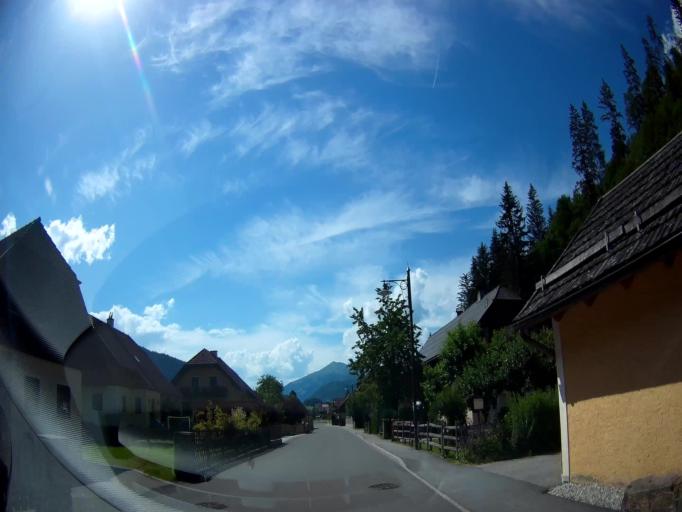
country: AT
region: Salzburg
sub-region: Politischer Bezirk Tamsweg
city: Thomatal
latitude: 47.0730
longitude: 13.7468
